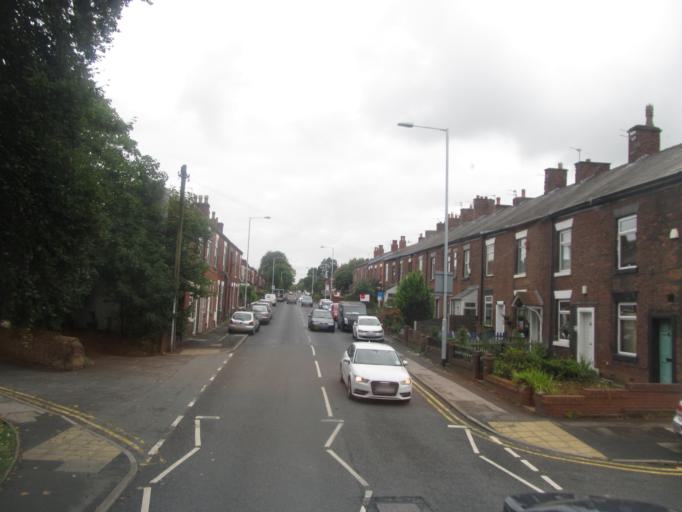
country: GB
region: England
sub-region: Borough of Tameside
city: Haughton Green
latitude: 53.4301
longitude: -2.0919
